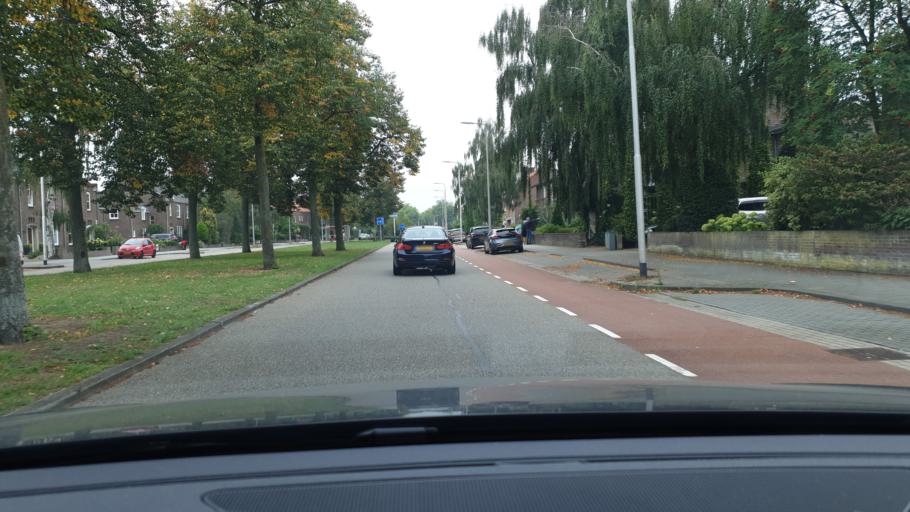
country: NL
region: North Brabant
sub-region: Gemeente Oss
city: Oss
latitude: 51.7637
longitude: 5.5135
